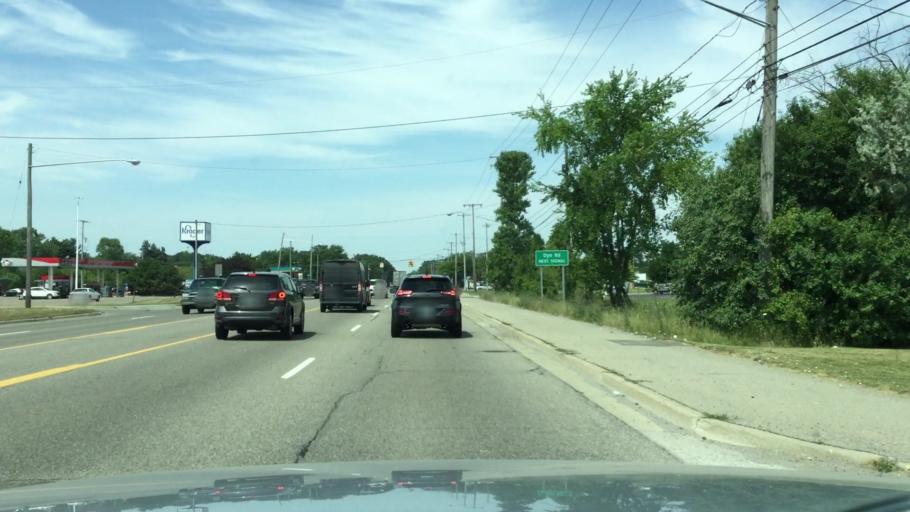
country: US
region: Michigan
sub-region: Genesee County
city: Swartz Creek
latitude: 43.0020
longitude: -83.7804
